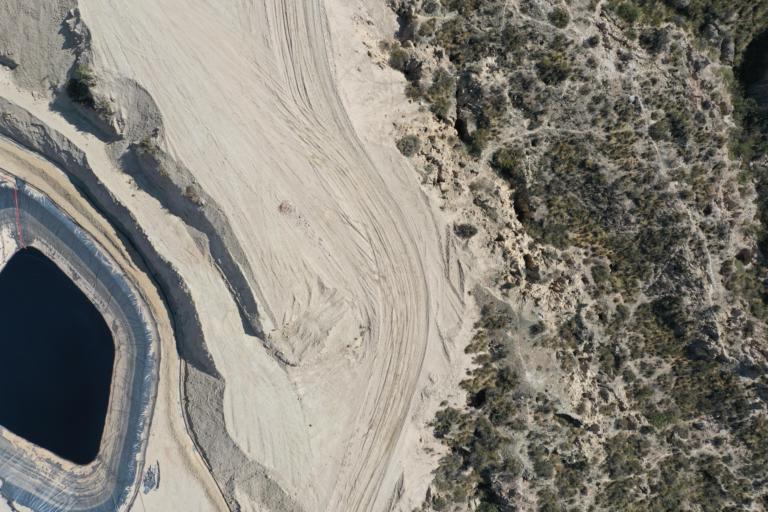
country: BO
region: La Paz
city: La Paz
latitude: -16.5612
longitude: -68.1251
